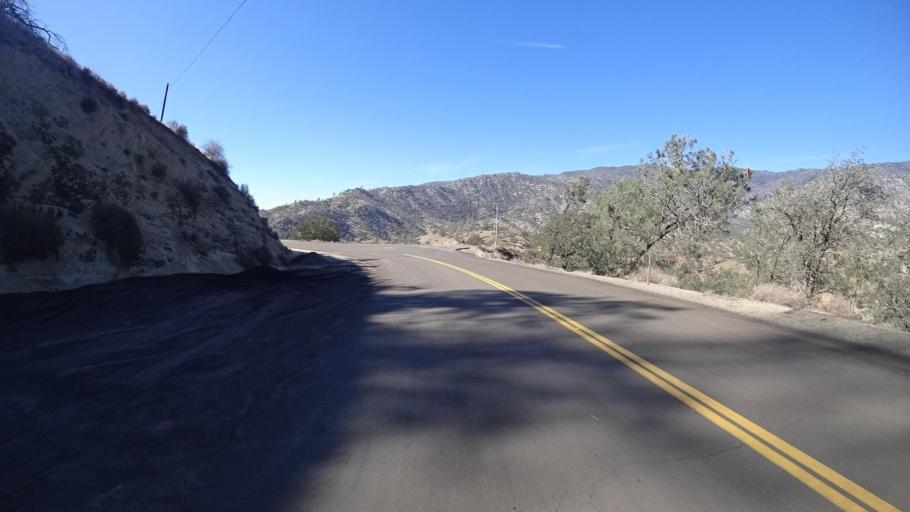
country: US
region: California
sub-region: Kern County
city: Bodfish
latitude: 35.5905
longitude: -118.5195
